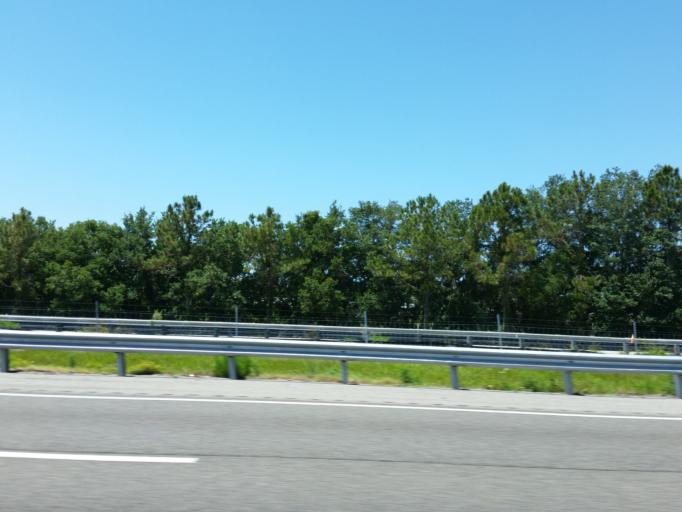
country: US
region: Florida
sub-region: Sarasota County
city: Nokomis
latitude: 27.1485
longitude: -82.4188
